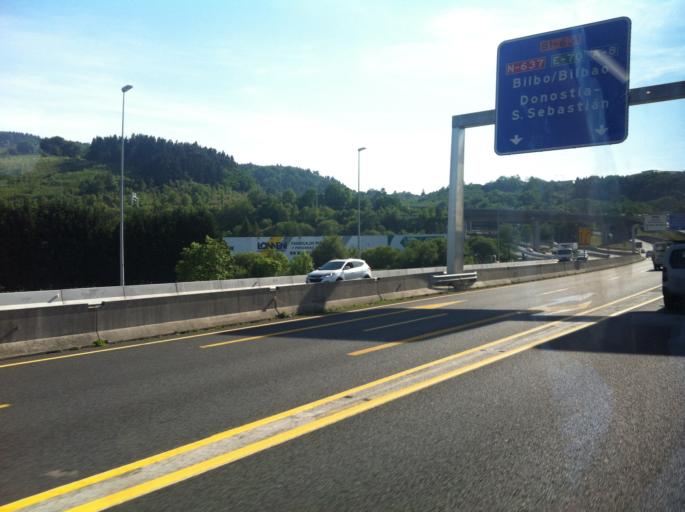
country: ES
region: Basque Country
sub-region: Bizkaia
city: Zamudio
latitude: 43.2871
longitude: -2.8854
